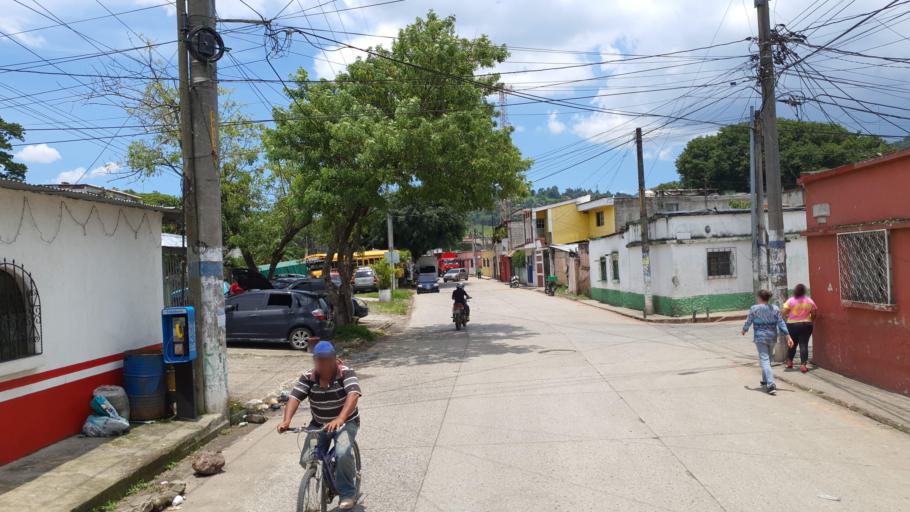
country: GT
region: Guatemala
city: Villa Canales
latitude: 14.4807
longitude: -90.5357
